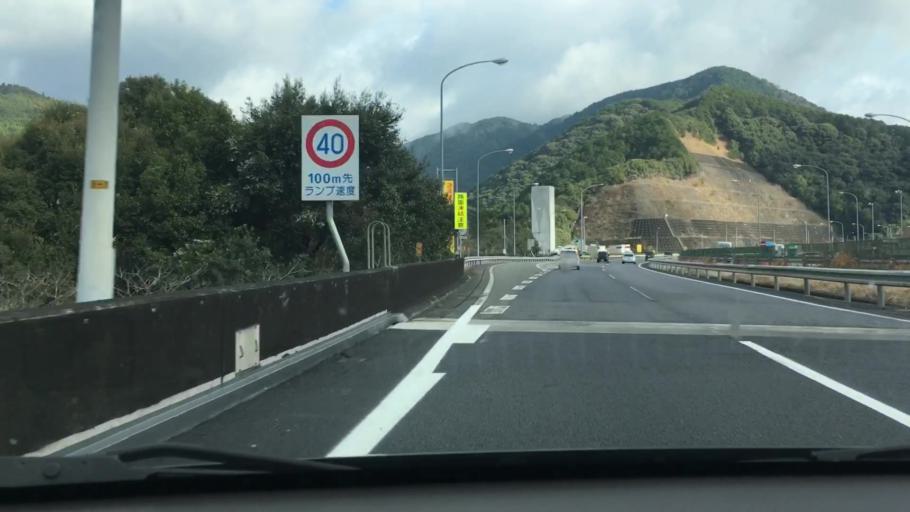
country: JP
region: Kumamoto
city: Yatsushiro
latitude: 32.4432
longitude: 130.6667
